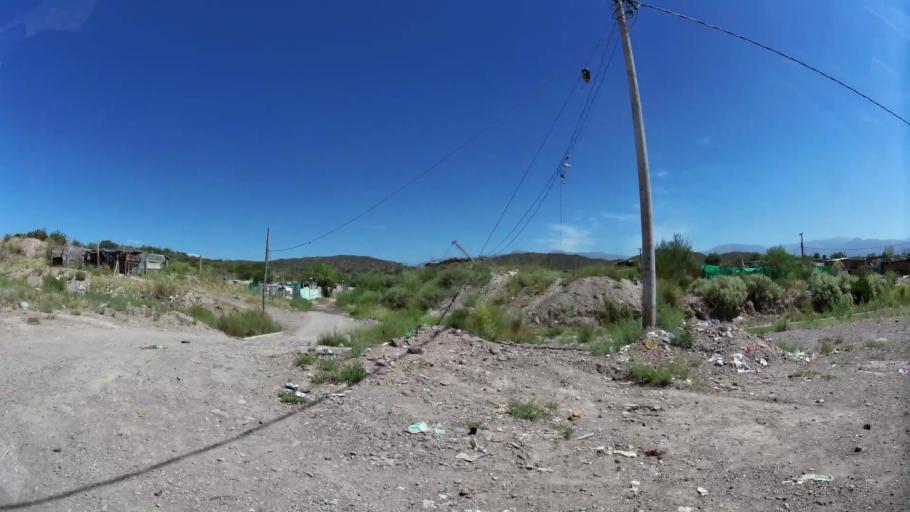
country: AR
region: Mendoza
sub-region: Departamento de Godoy Cruz
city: Godoy Cruz
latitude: -32.9470
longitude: -68.8762
